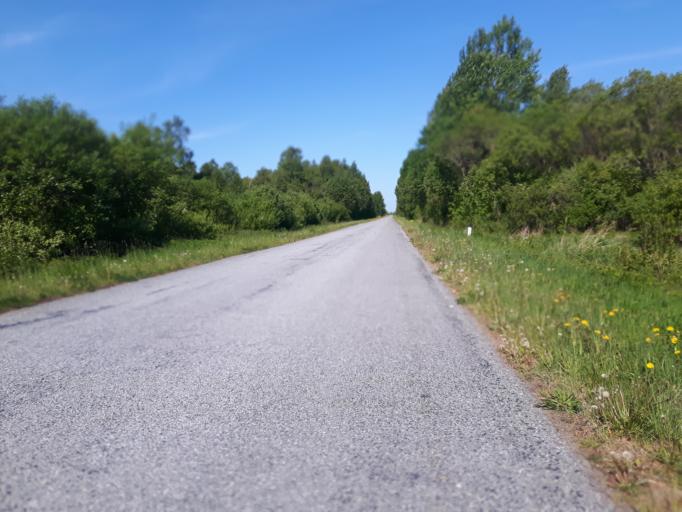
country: EE
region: Ida-Virumaa
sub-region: Aseri vald
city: Aseri
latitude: 59.4551
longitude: 26.8467
